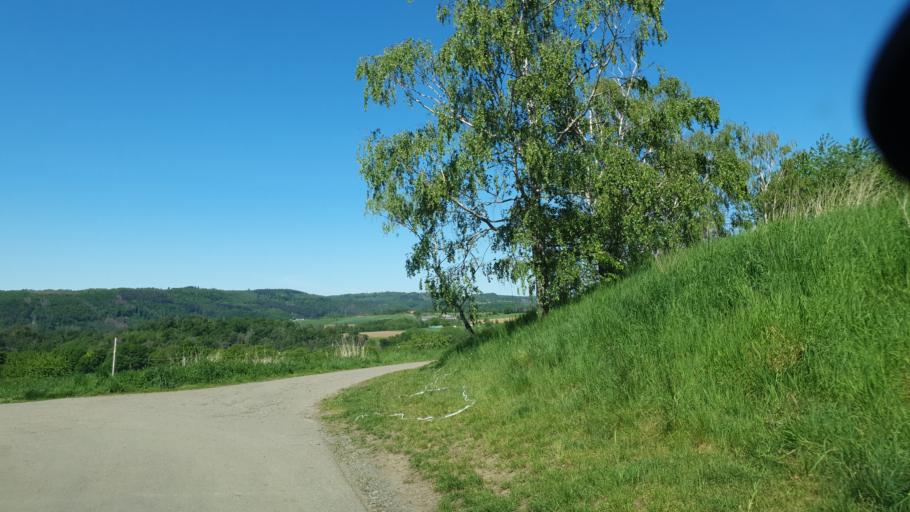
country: DE
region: Rheinland-Pfalz
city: Frucht
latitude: 50.3156
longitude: 7.6732
